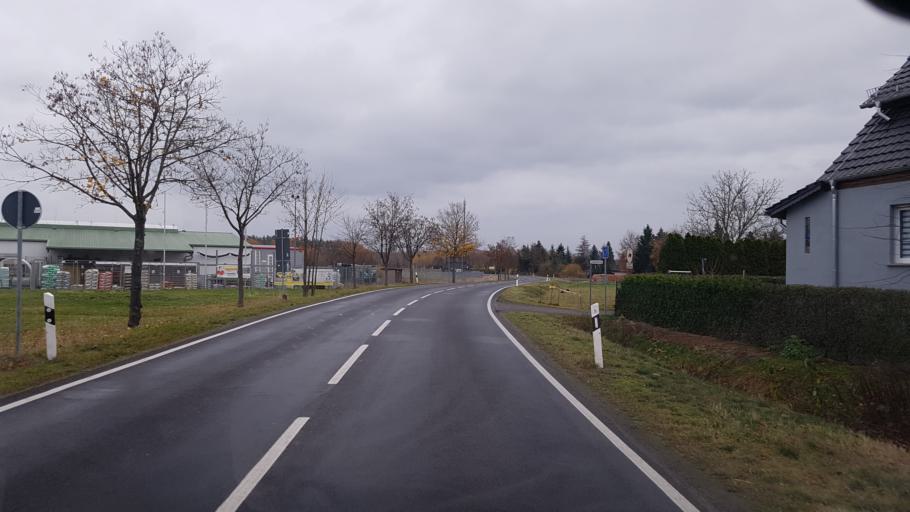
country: DE
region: Brandenburg
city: Ortrand
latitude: 51.3829
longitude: 13.7613
